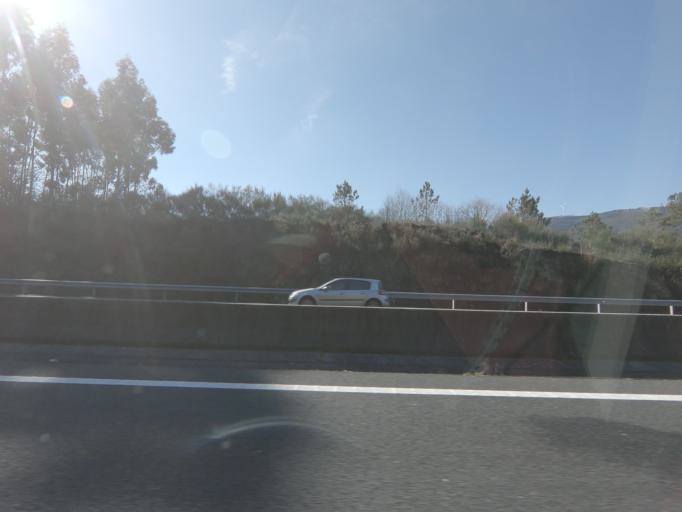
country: ES
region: Galicia
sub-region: Provincia de Ourense
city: Pinor
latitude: 42.4929
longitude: -8.0253
